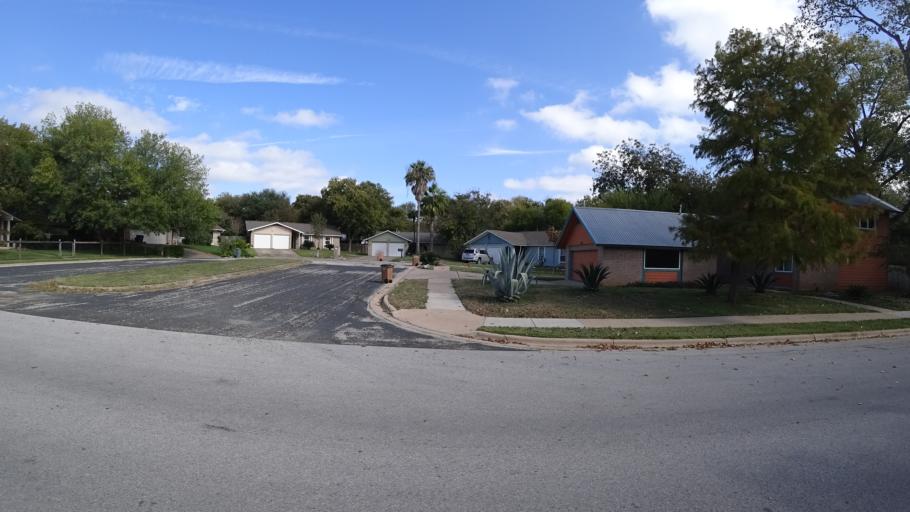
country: US
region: Texas
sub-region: Travis County
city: Shady Hollow
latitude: 30.1926
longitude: -97.8170
